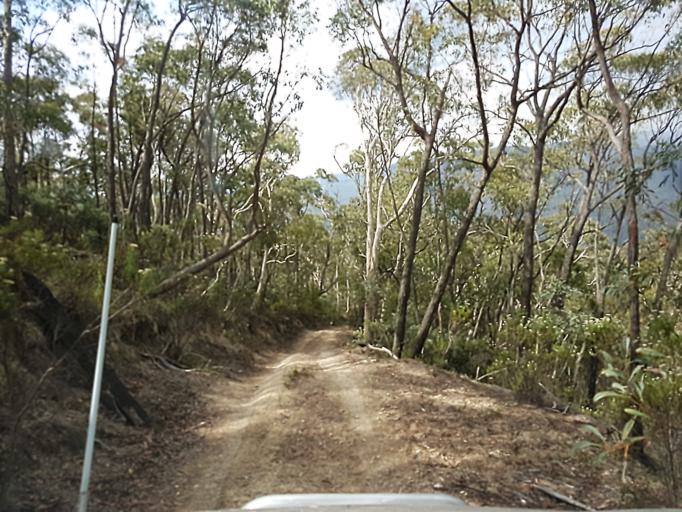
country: AU
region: New South Wales
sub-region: Snowy River
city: Jindabyne
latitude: -36.8785
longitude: 148.2169
